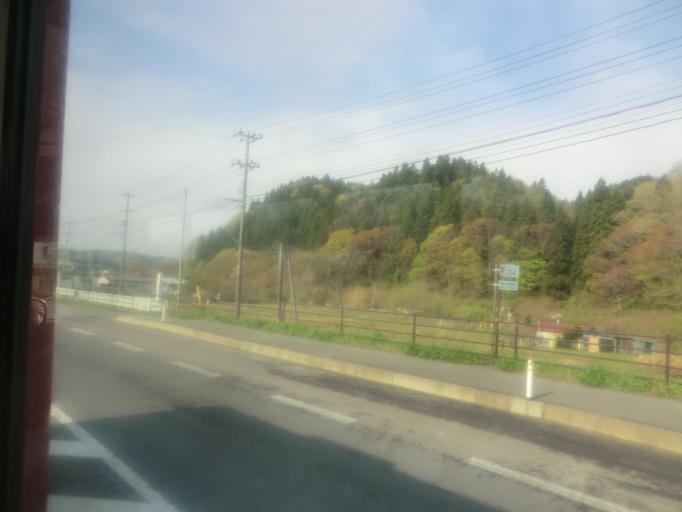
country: JP
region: Iwate
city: Miyako
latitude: 39.5703
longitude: 141.9330
